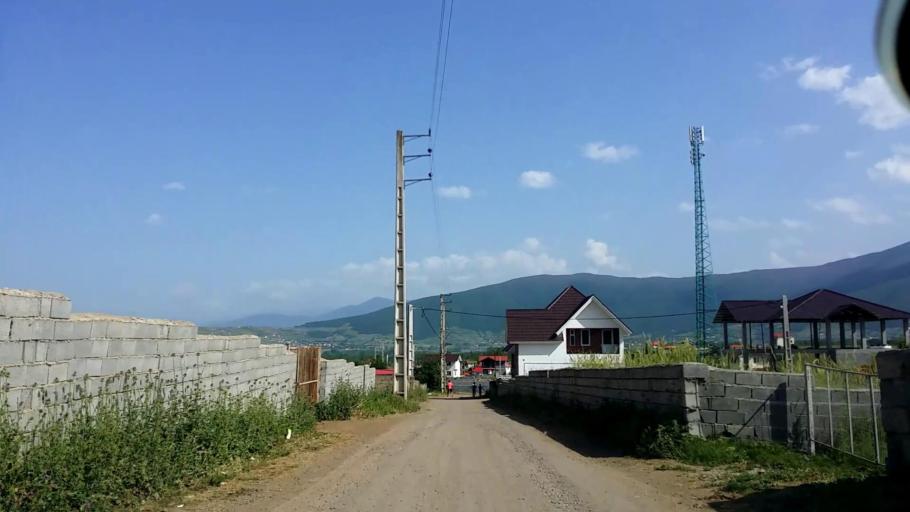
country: IR
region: Mazandaran
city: `Abbasabad
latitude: 36.5463
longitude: 51.1864
